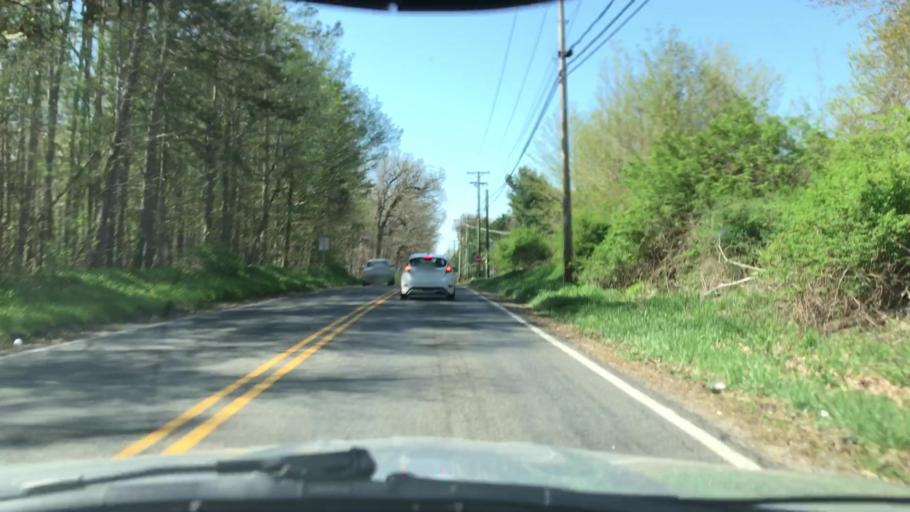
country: US
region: Indiana
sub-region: Saint Joseph County
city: Georgetown
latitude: 41.7437
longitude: -86.2972
